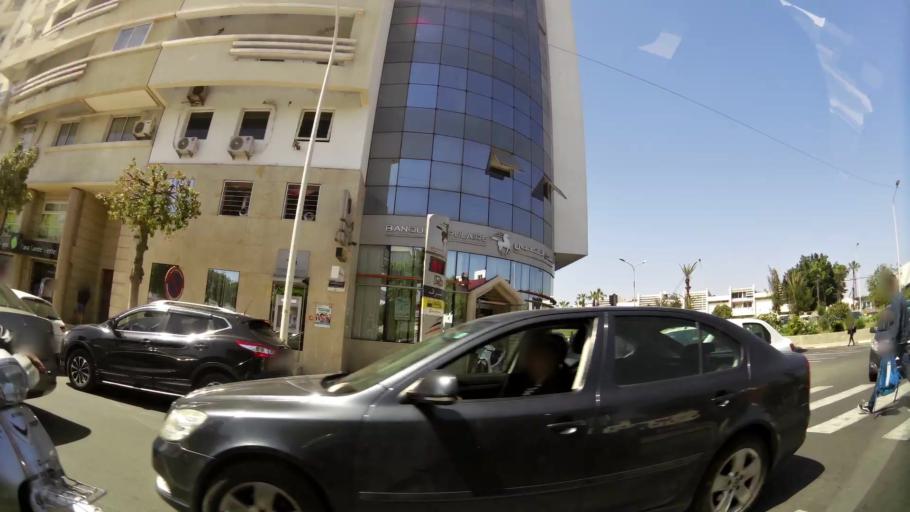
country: MA
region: Souss-Massa-Draa
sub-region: Agadir-Ida-ou-Tnan
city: Agadir
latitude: 30.4143
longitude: -9.5854
